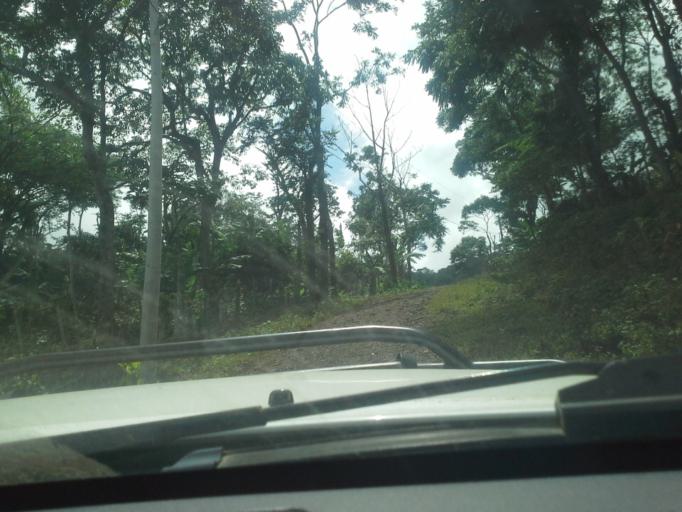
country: NI
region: Boaco
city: San Jose de los Remates
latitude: 12.6934
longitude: -85.7351
